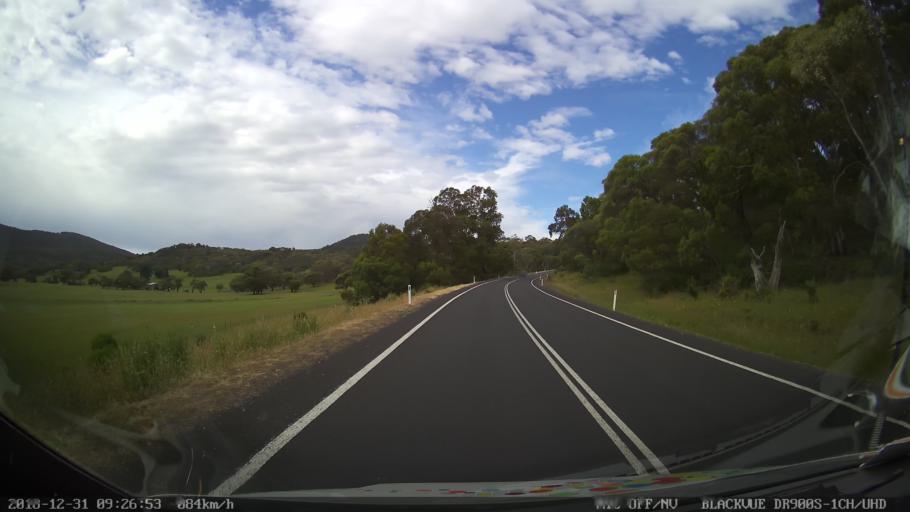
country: AU
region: New South Wales
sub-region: Snowy River
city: Jindabyne
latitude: -36.4530
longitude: 148.4922
